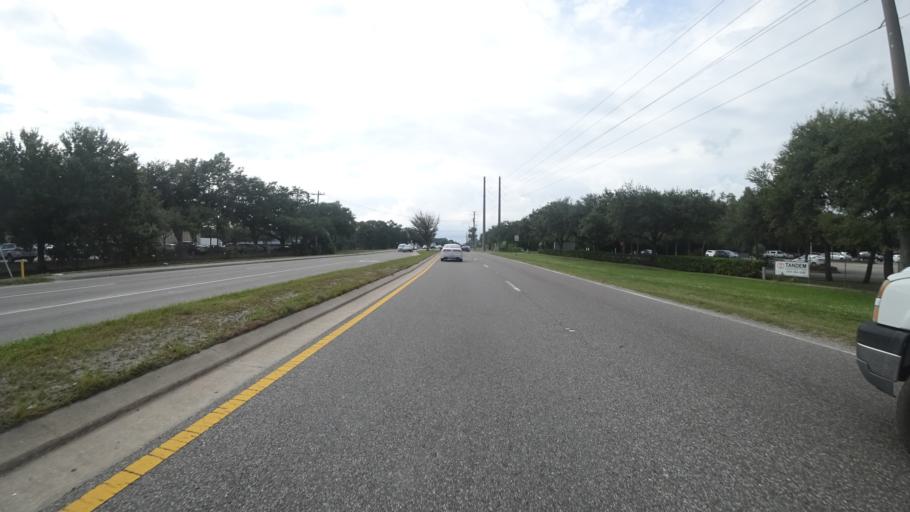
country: US
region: Florida
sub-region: Manatee County
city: Whitfield
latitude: 27.4292
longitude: -82.5311
